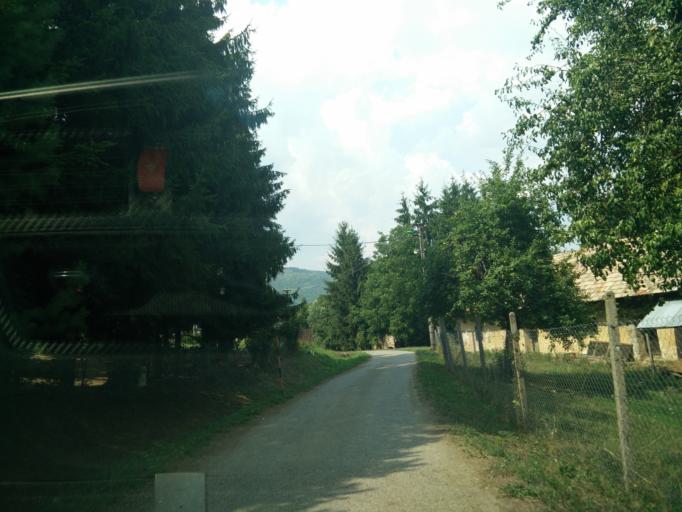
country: SK
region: Banskobystricky
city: Ziar nad Hronom
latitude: 48.5772
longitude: 18.7634
